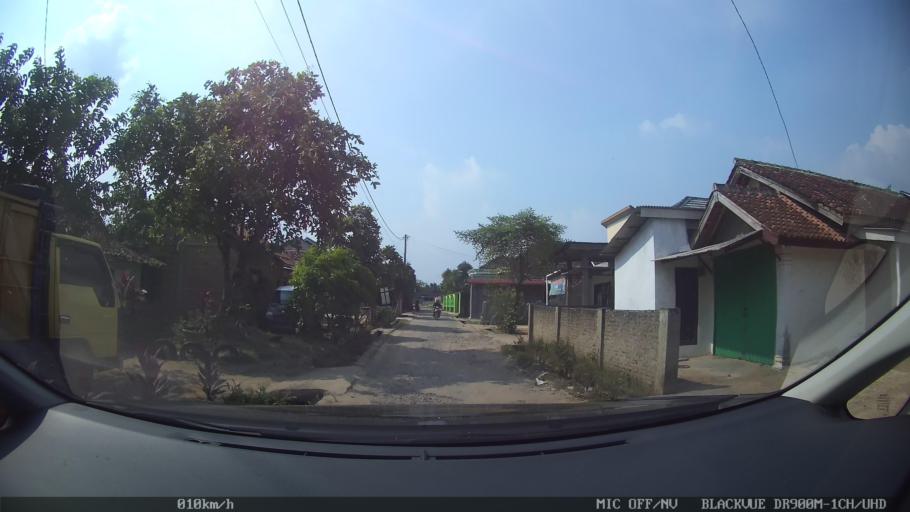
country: ID
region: Lampung
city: Natar
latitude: -5.3111
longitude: 105.2025
